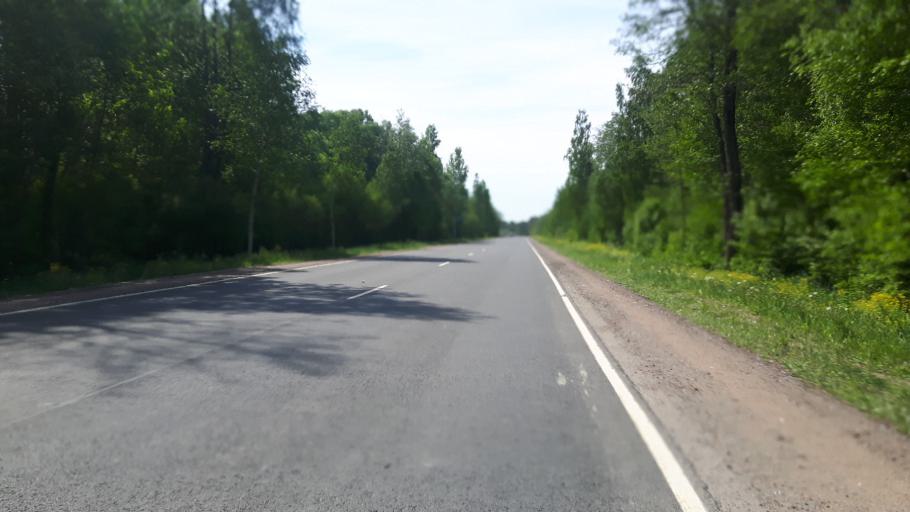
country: RU
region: Leningrad
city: Vistino
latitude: 59.6778
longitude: 28.4537
